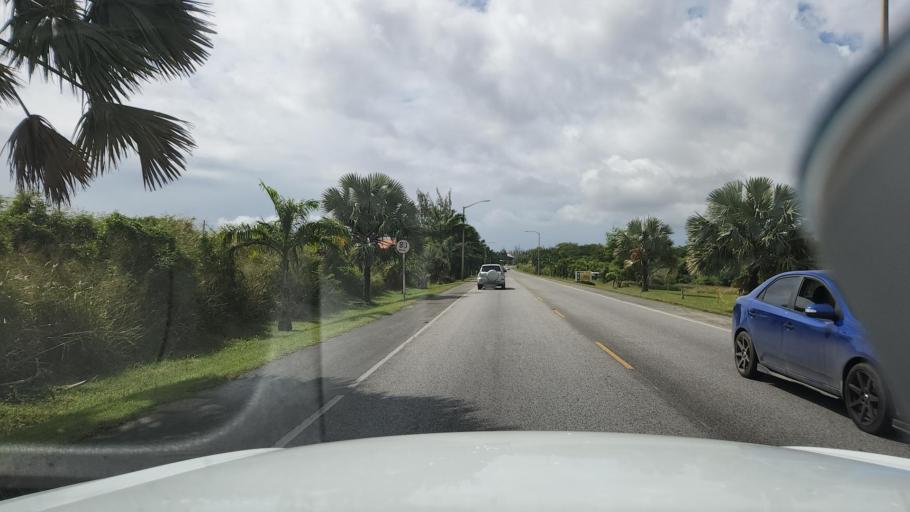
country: BB
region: Christ Church
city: Oistins
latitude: 13.0791
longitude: -59.5200
